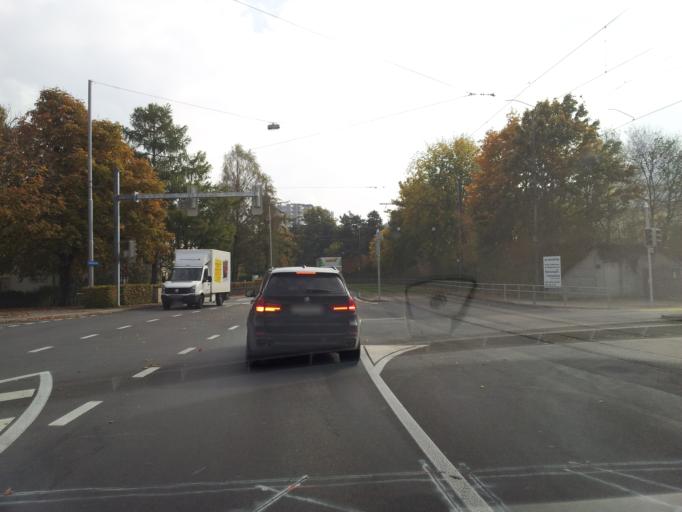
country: CH
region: Bern
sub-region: Bern-Mittelland District
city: Bern
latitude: 46.9340
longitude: 7.4400
